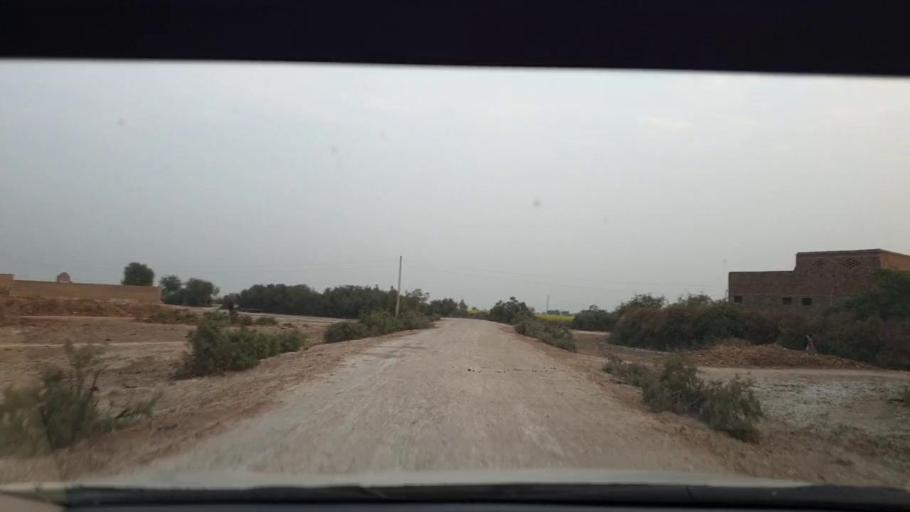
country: PK
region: Sindh
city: Berani
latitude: 25.8798
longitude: 68.7558
